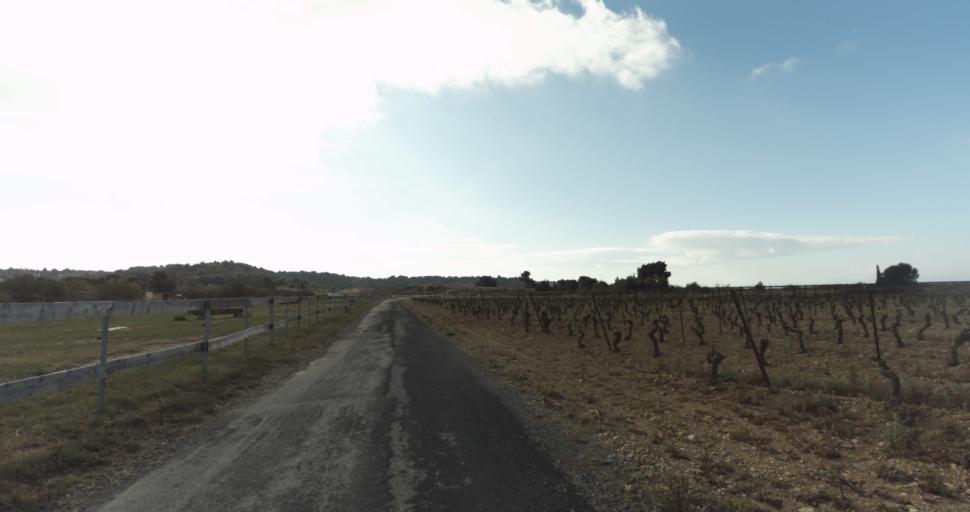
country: FR
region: Languedoc-Roussillon
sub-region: Departement de l'Aude
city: Leucate
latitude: 42.9309
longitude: 3.0063
